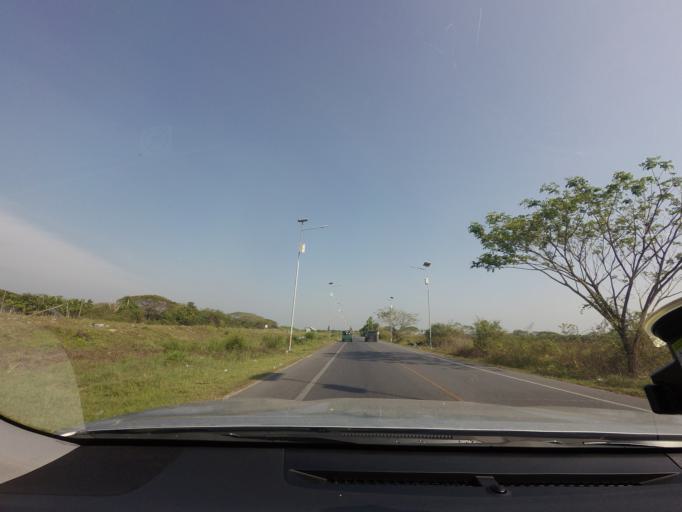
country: TH
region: Nakhon Si Thammarat
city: Nakhon Si Thammarat
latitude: 8.4573
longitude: 99.9803
